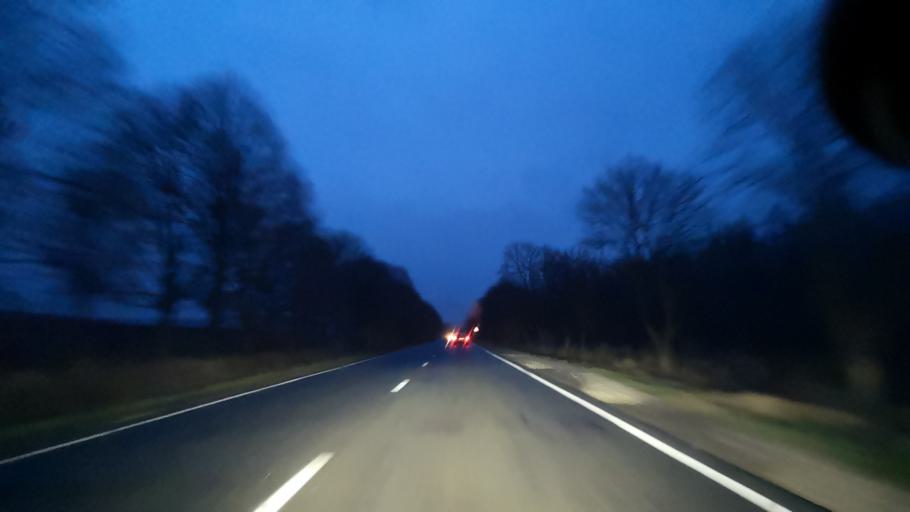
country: MD
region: Orhei
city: Orhei
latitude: 47.4763
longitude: 28.7918
